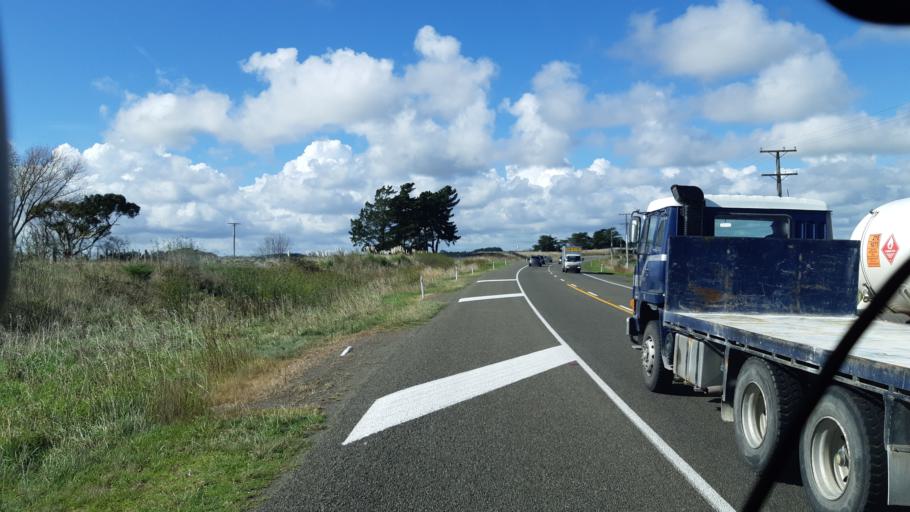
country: NZ
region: Manawatu-Wanganui
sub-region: Wanganui District
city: Wanganui
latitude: -39.9749
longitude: 175.1247
